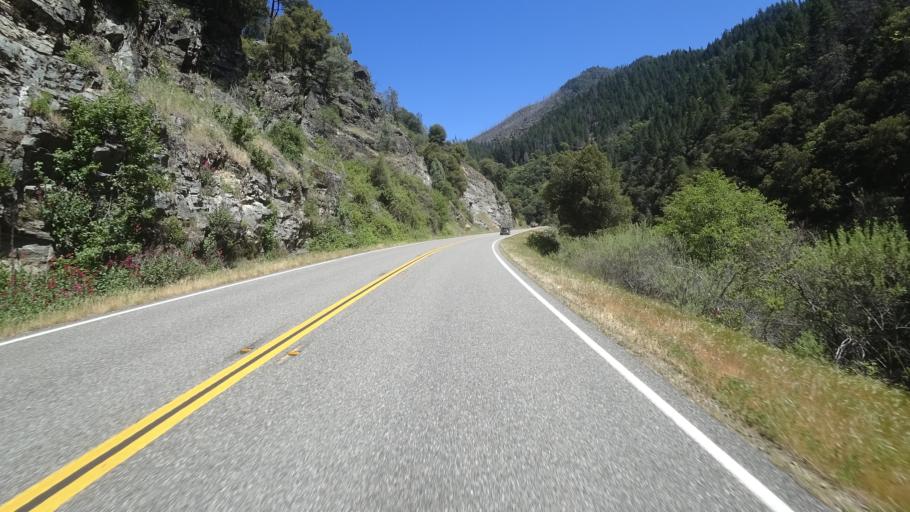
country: US
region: California
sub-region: Trinity County
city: Hayfork
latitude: 40.7520
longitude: -123.1636
